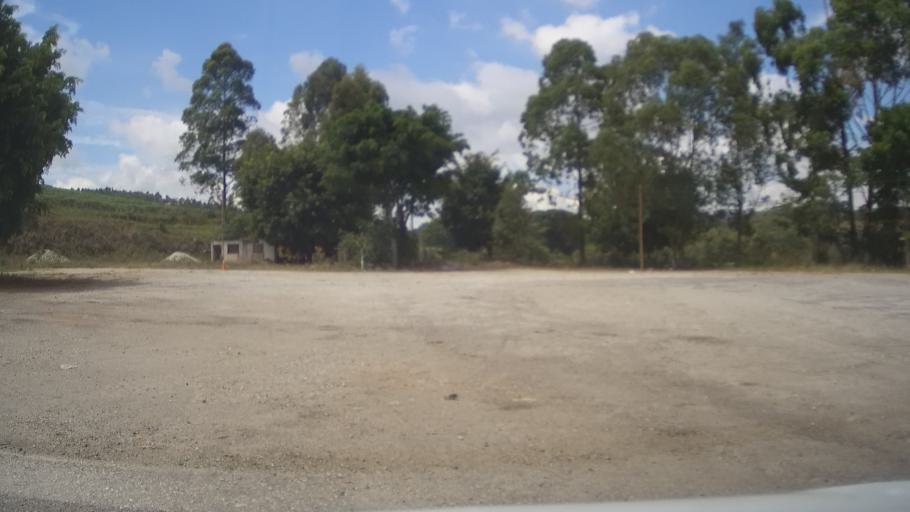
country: BR
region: Minas Gerais
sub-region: Santa Rita Do Sapucai
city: Santa Rita do Sapucai
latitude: -22.0942
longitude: -45.7110
